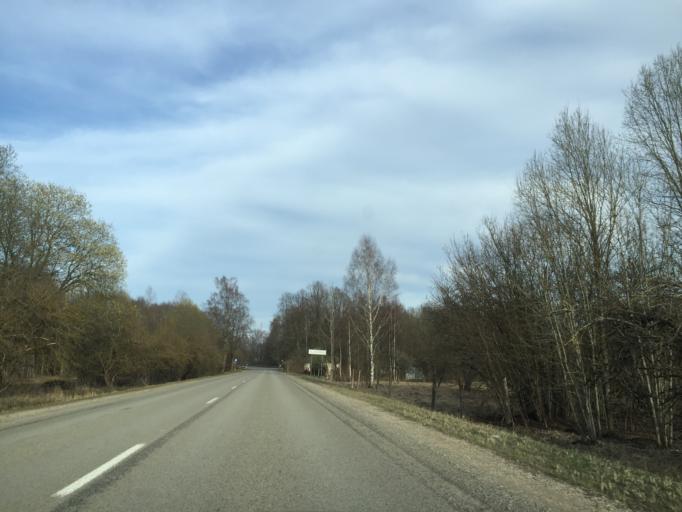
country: LV
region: Lielvarde
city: Lielvarde
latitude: 56.8004
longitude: 24.8570
